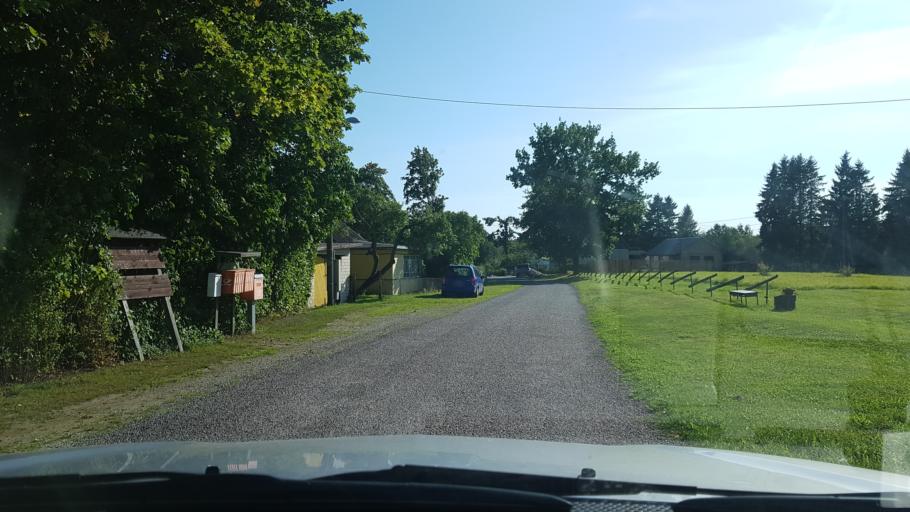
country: EE
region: Ida-Virumaa
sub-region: Narva-Joesuu linn
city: Narva-Joesuu
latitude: 59.4037
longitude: 28.0025
